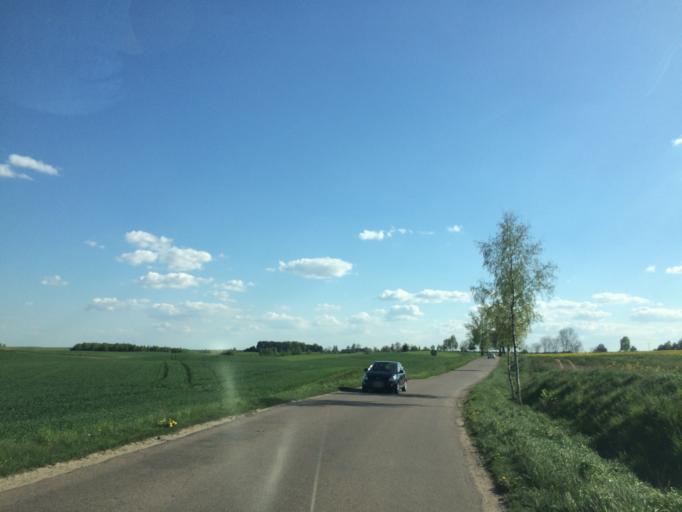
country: PL
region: Warmian-Masurian Voivodeship
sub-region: Powiat dzialdowski
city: Rybno
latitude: 53.4112
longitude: 19.9381
